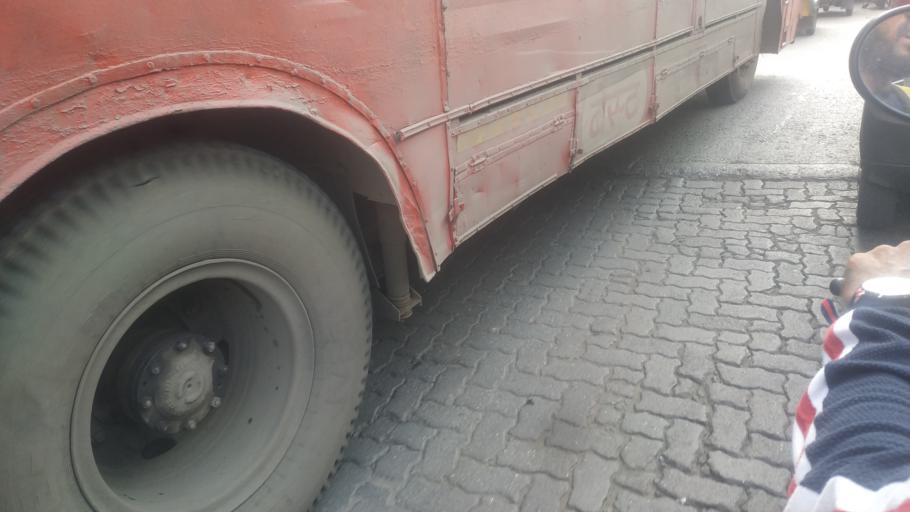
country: IN
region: Maharashtra
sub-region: Mumbai Suburban
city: Mumbai
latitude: 19.0463
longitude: 72.8631
